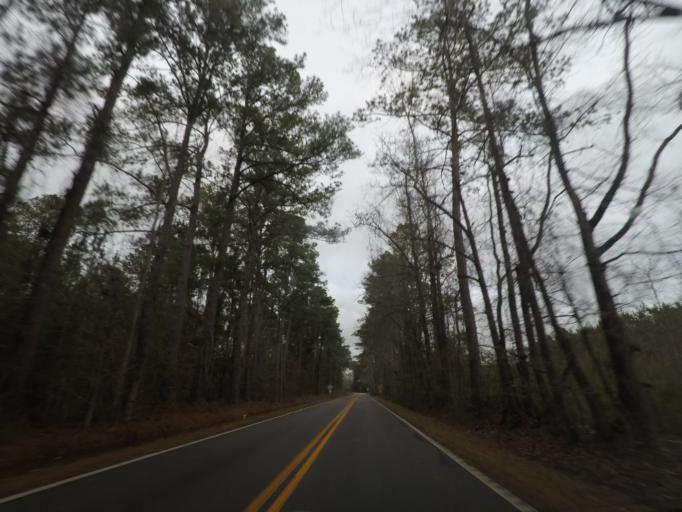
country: US
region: South Carolina
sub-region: Colleton County
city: Walterboro
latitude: 32.8993
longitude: -80.5153
